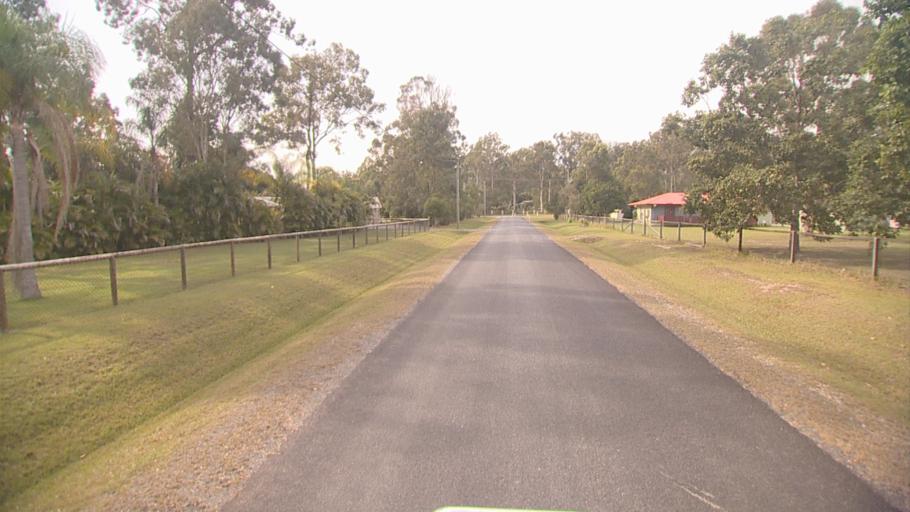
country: AU
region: Queensland
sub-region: Logan
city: Waterford West
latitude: -27.7329
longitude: 153.1363
